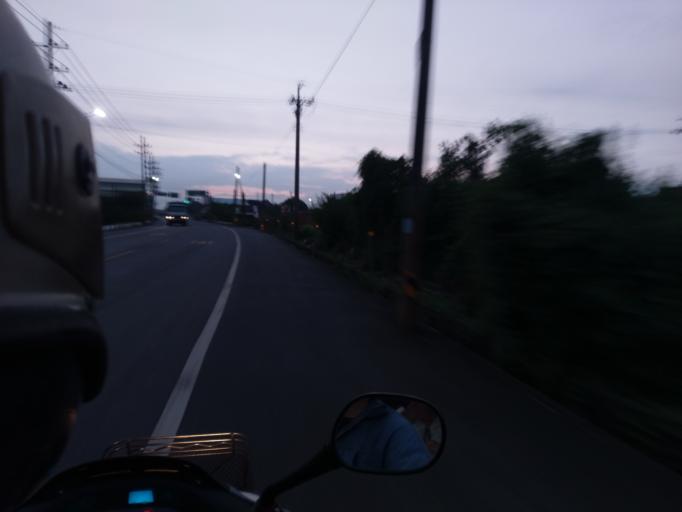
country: TW
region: Taiwan
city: Xinying
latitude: 23.1929
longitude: 120.3267
